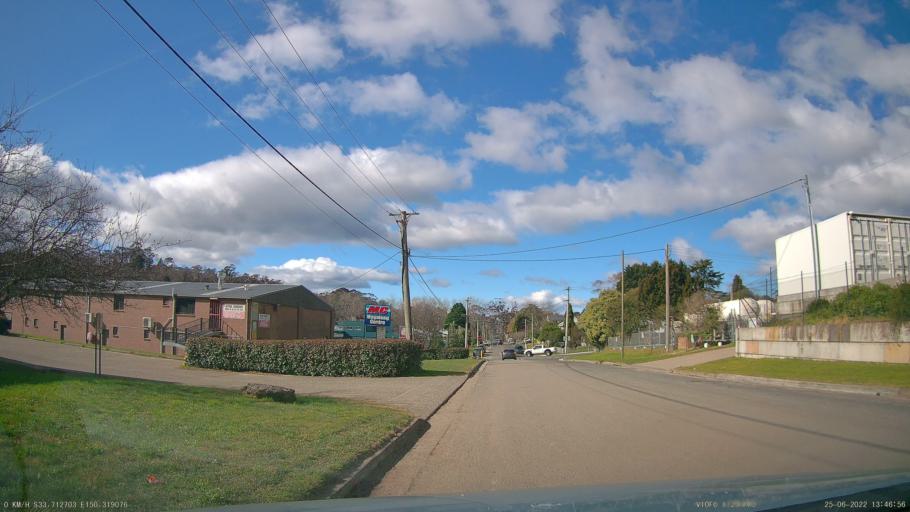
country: AU
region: New South Wales
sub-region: Blue Mountains Municipality
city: Katoomba
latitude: -33.7127
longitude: 150.3190
